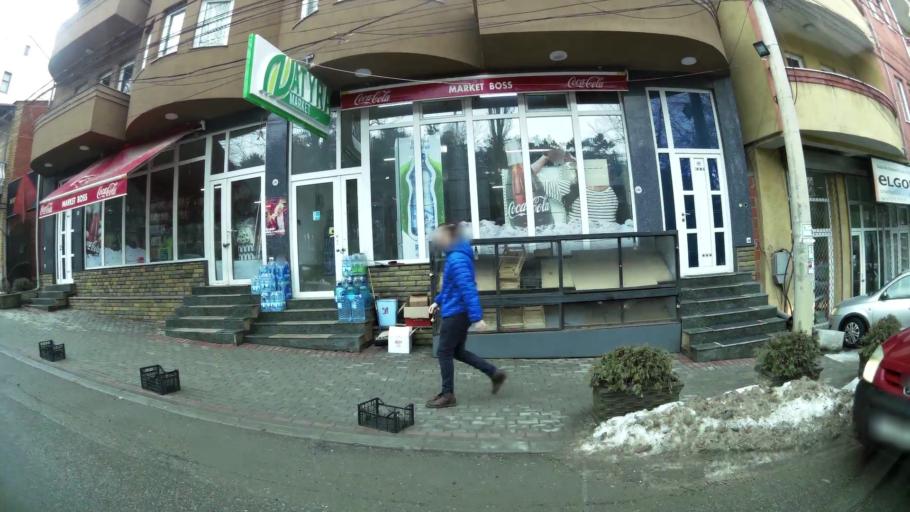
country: XK
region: Pristina
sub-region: Komuna e Prishtines
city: Pristina
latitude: 42.6604
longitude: 21.1687
